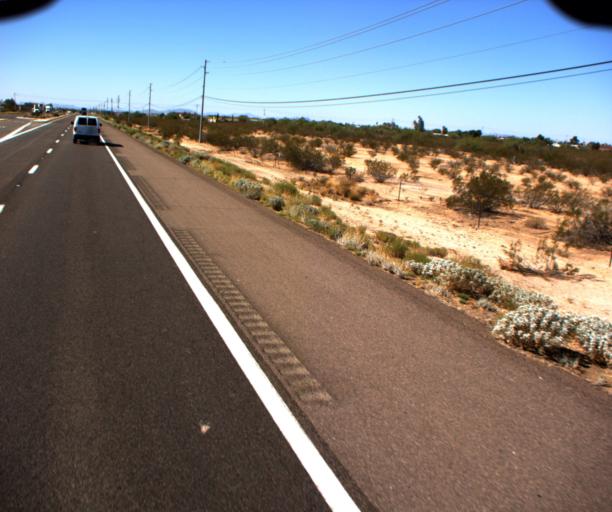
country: US
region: Arizona
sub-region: Pinal County
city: Casa Grande
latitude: 32.9787
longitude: -111.7569
